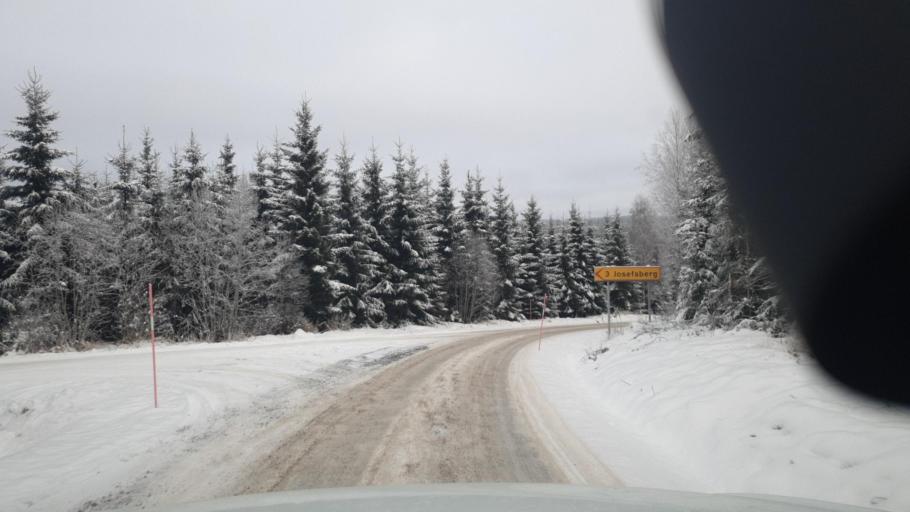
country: SE
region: Vaermland
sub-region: Torsby Kommun
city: Torsby
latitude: 60.1857
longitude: 12.6450
